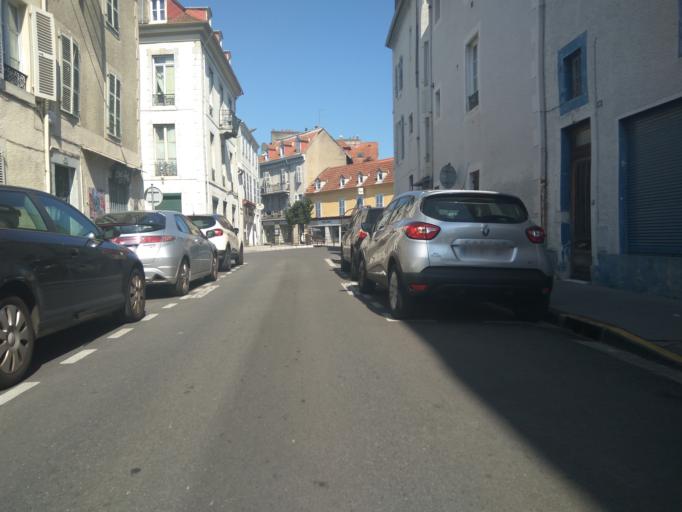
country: FR
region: Aquitaine
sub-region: Departement des Pyrenees-Atlantiques
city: Pau
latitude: 43.3010
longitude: -0.3735
